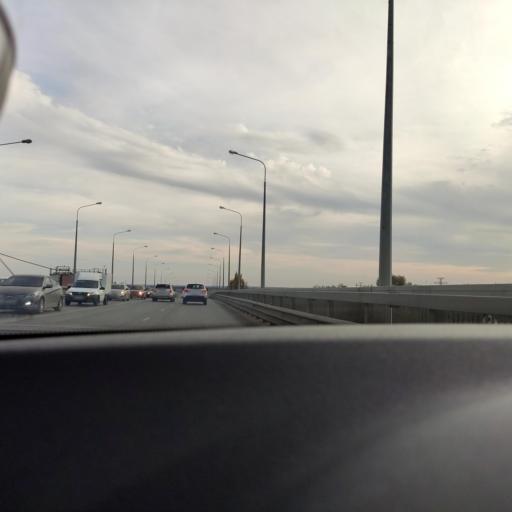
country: RU
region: Samara
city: Samara
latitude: 53.1764
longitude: 50.1935
